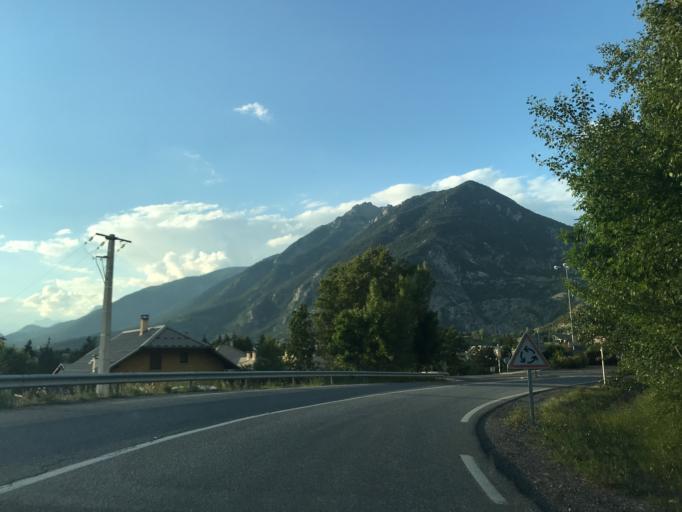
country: FR
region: Provence-Alpes-Cote d'Azur
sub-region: Departement des Hautes-Alpes
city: Guillestre
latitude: 44.6554
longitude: 6.6539
